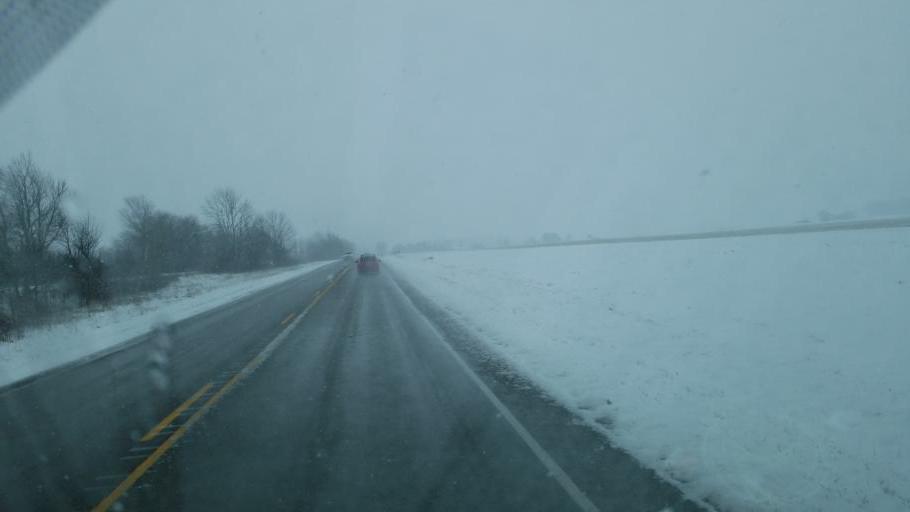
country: US
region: Indiana
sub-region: Wayne County
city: Hagerstown
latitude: 40.0387
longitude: -85.2082
